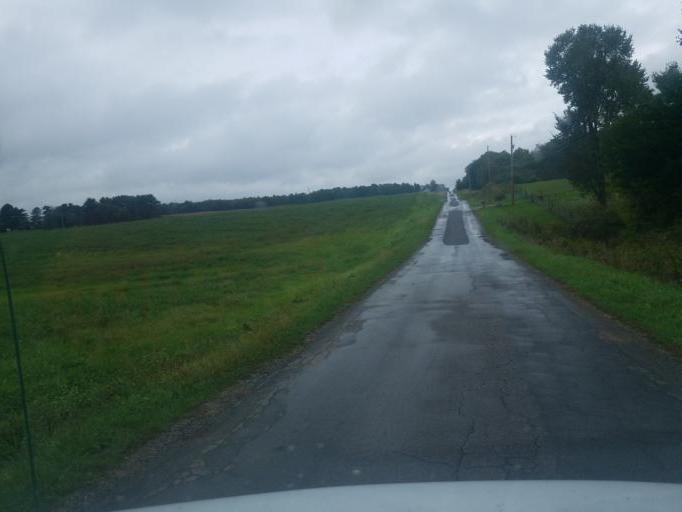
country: US
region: Ohio
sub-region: Wayne County
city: West Salem
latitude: 40.9300
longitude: -82.1380
